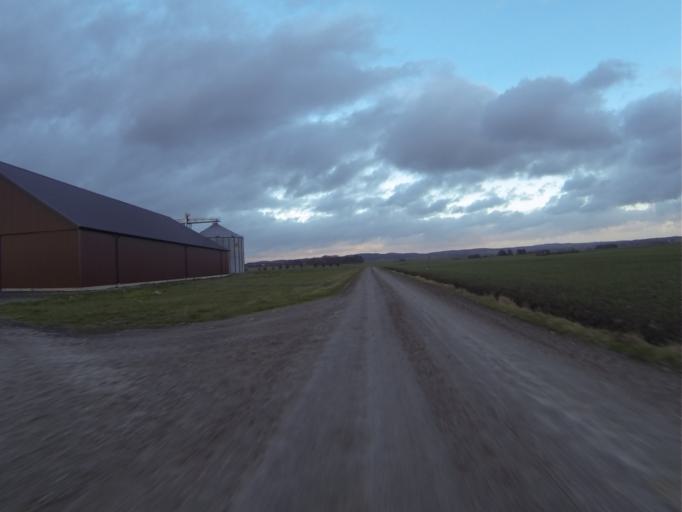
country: SE
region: Skane
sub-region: Lunds Kommun
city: Genarp
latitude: 55.6227
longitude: 13.3470
